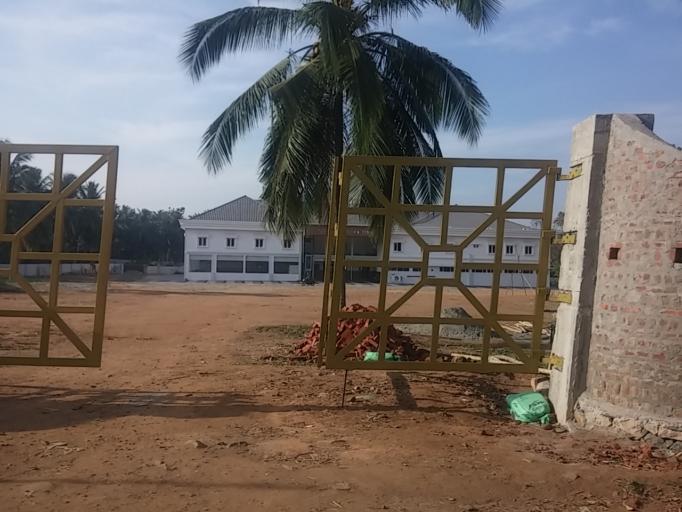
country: IN
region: Kerala
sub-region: Thrissur District
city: Chelakara
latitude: 10.5973
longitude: 76.4996
